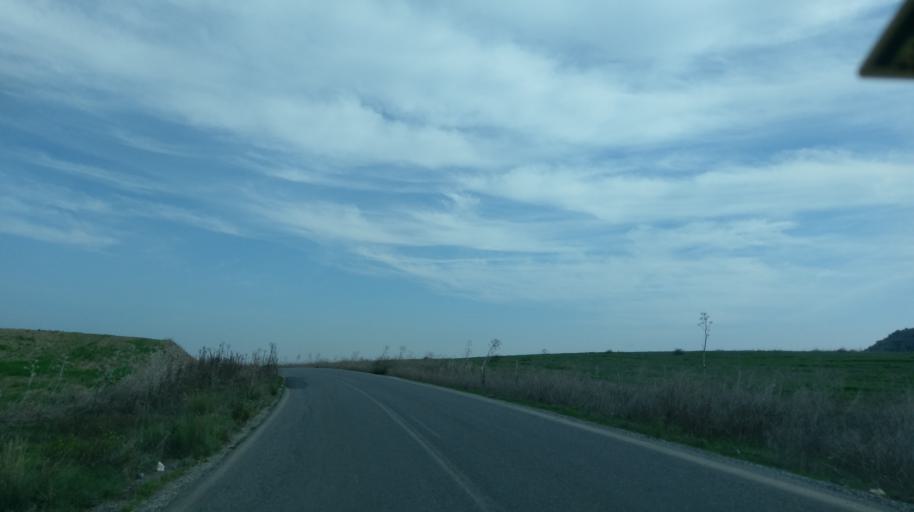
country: CY
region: Keryneia
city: Lapithos
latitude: 35.2561
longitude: 33.1374
